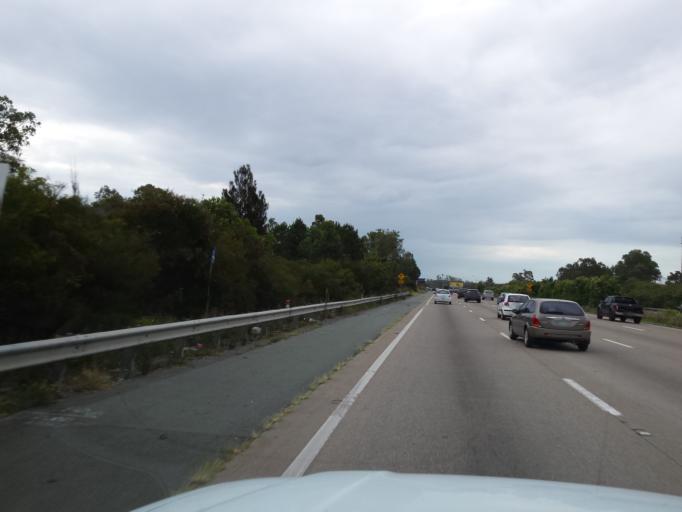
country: AU
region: Queensland
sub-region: Gold Coast
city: Oxenford
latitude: -27.8725
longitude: 153.3135
